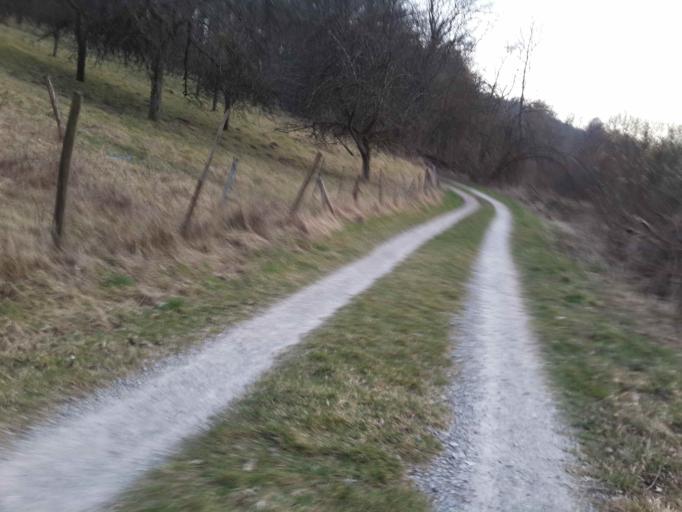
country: DE
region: Baden-Wuerttemberg
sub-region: Karlsruhe Region
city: Neckargerach
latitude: 49.3841
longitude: 9.0825
